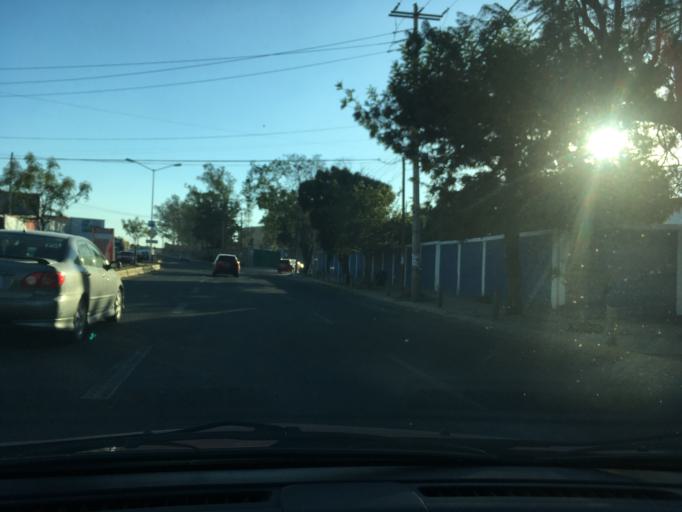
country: MX
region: Jalisco
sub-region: Tlajomulco de Zuniga
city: La Tijera
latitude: 20.5929
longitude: -103.4127
